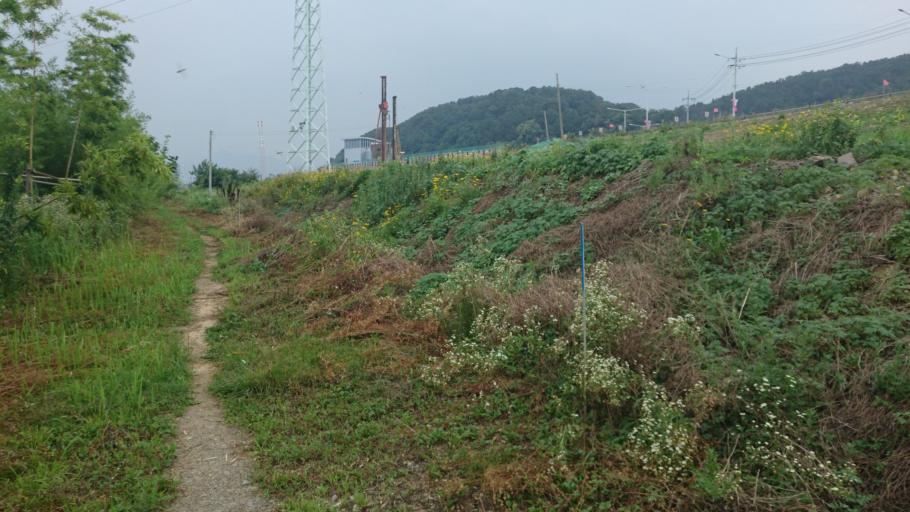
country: KR
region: Daegu
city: Hwawon
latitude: 35.8512
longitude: 128.4699
